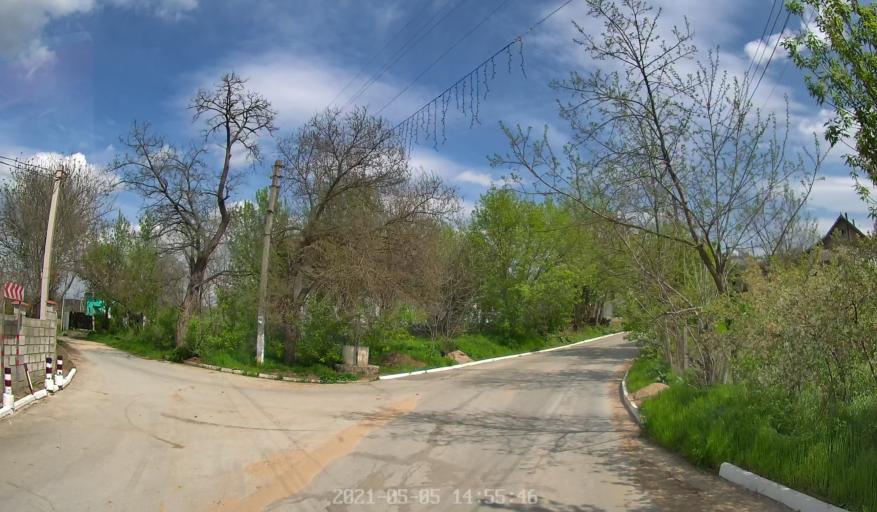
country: MD
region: Chisinau
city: Vadul lui Voda
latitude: 47.0995
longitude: 29.1721
